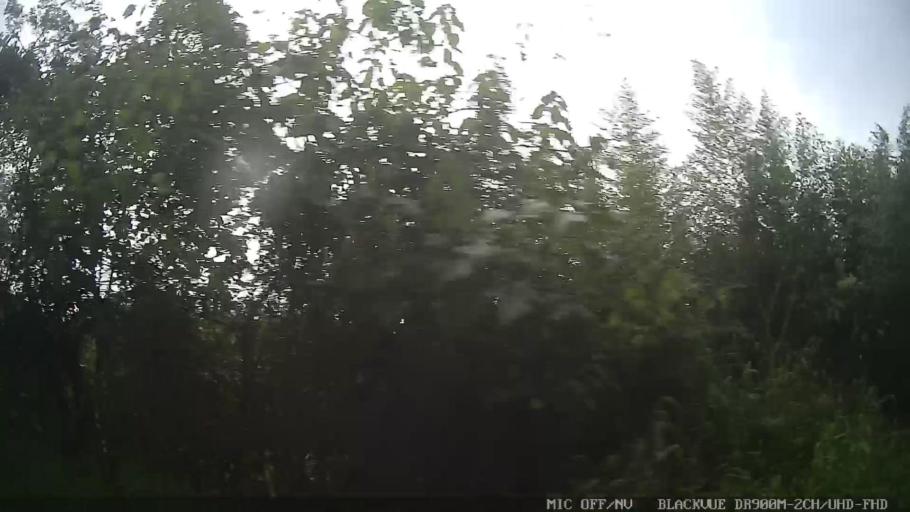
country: BR
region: Sao Paulo
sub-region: Ribeirao Pires
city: Ribeirao Pires
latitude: -23.6988
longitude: -46.3676
